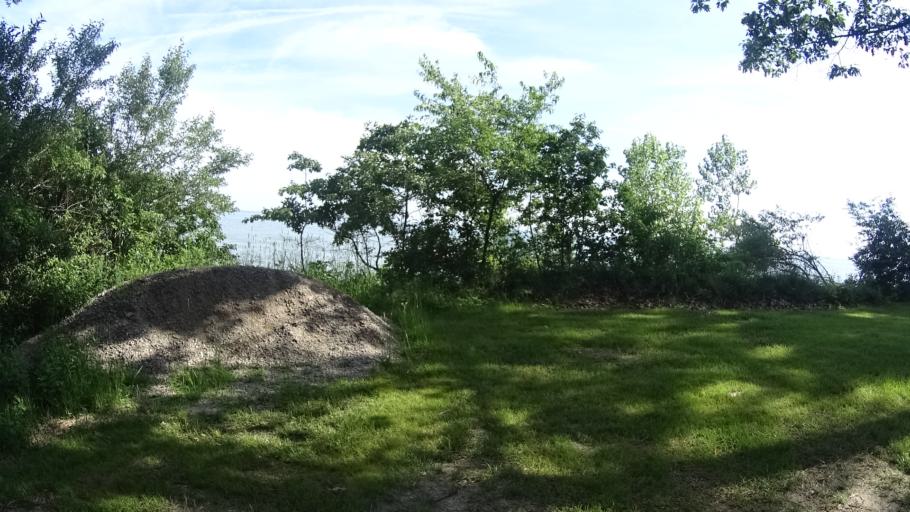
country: US
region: Ohio
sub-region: Erie County
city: Huron
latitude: 41.3833
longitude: -82.5108
